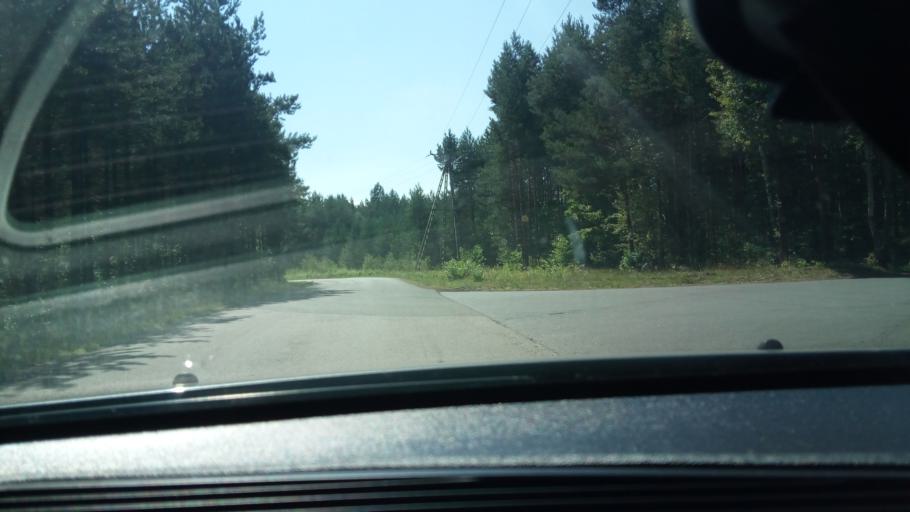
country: PL
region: Lesser Poland Voivodeship
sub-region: Powiat chrzanowski
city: Zarki
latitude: 50.1060
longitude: 19.3657
